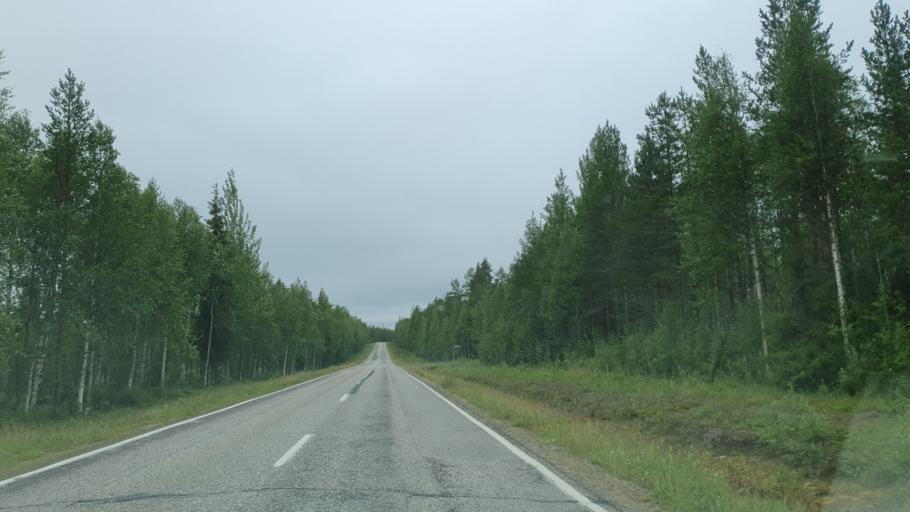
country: FI
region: Lapland
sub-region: Itae-Lappi
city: Pyhaejaervi
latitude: 67.3528
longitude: 27.0057
